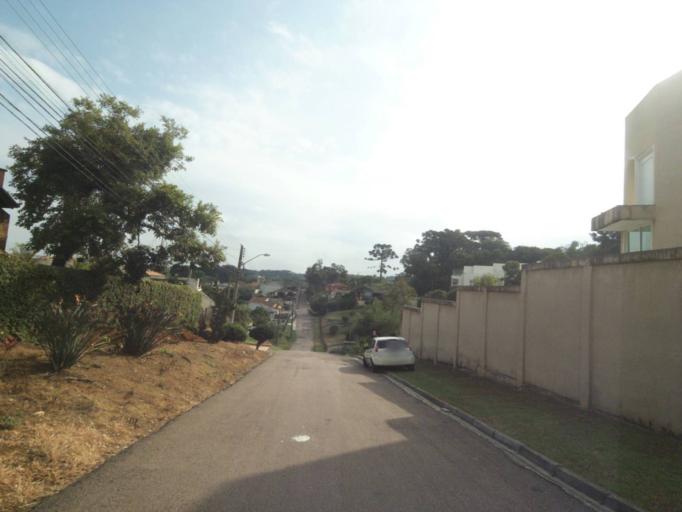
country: BR
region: Parana
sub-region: Curitiba
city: Curitiba
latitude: -25.4108
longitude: -49.3103
